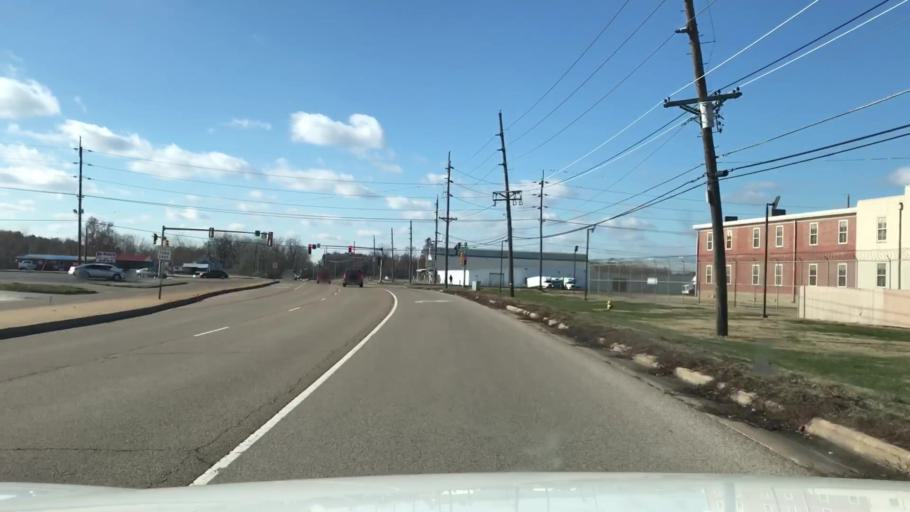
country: US
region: Illinois
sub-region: Saint Clair County
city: Washington Park
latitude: 38.6159
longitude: -90.0914
